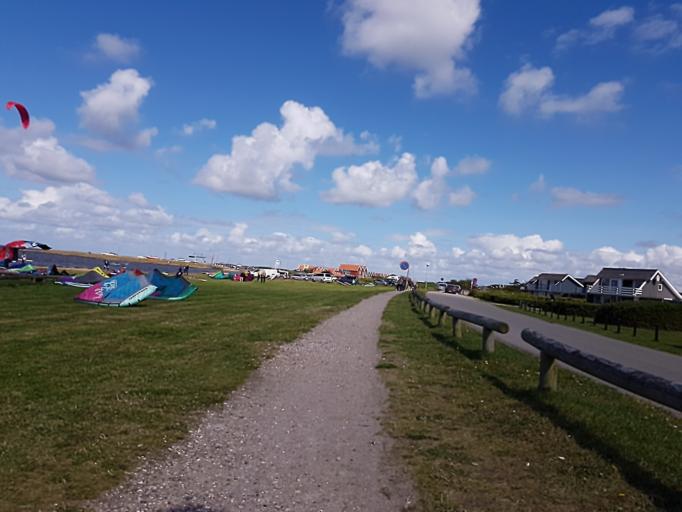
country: DK
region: Central Jutland
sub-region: Ringkobing-Skjern Kommune
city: Hvide Sande
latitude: 55.8454
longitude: 8.2761
